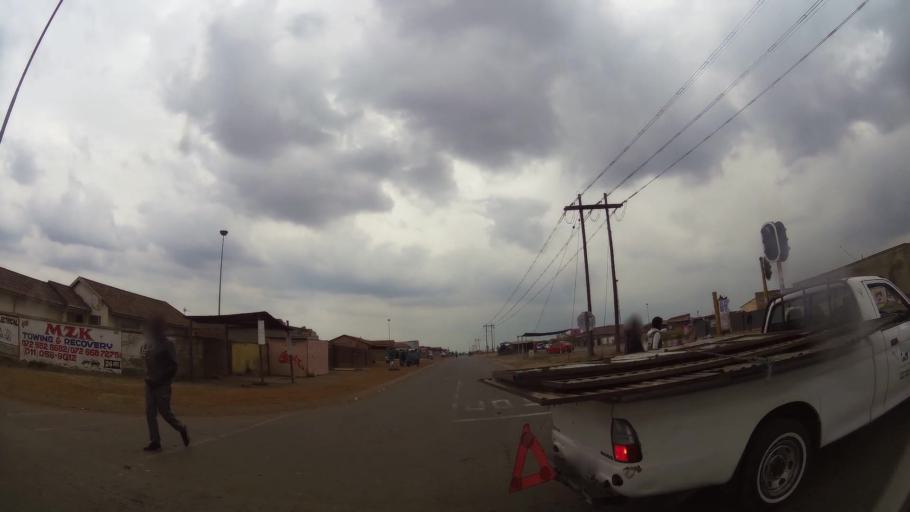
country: ZA
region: Gauteng
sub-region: Ekurhuleni Metropolitan Municipality
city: Germiston
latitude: -26.3590
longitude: 28.1499
